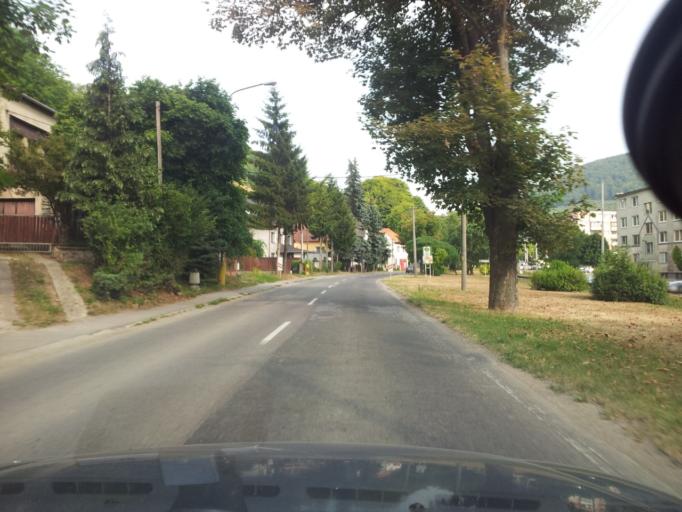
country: SK
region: Nitriansky
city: Trencianske Teplice
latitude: 48.9142
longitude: 18.1612
